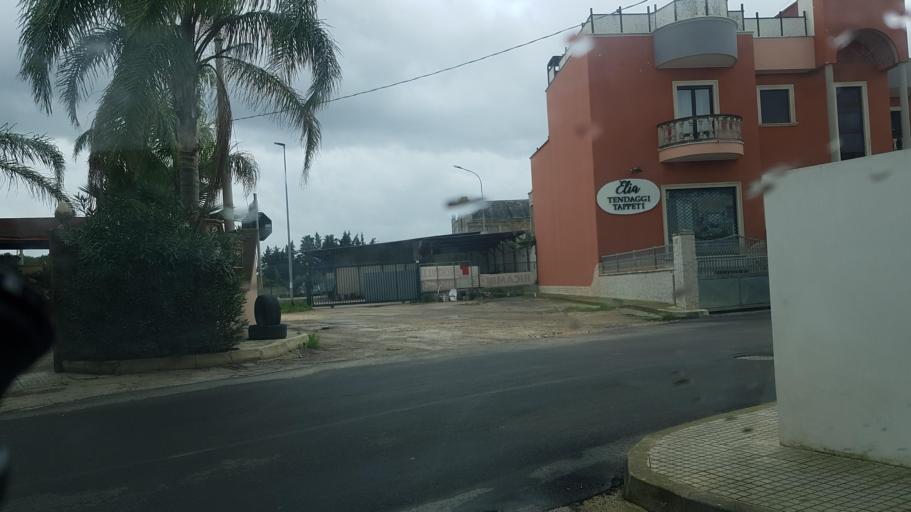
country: IT
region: Apulia
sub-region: Provincia di Lecce
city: Carmiano
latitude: 40.3508
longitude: 18.0459
